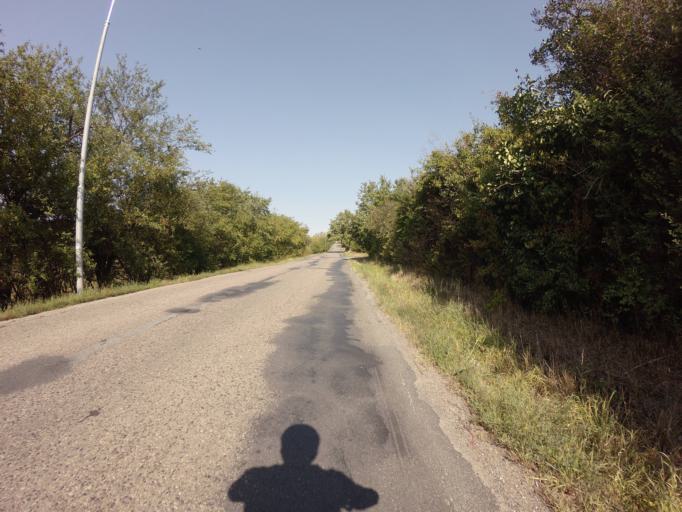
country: CZ
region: Central Bohemia
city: Tynec nad Sazavou
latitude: 49.8435
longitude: 14.5598
